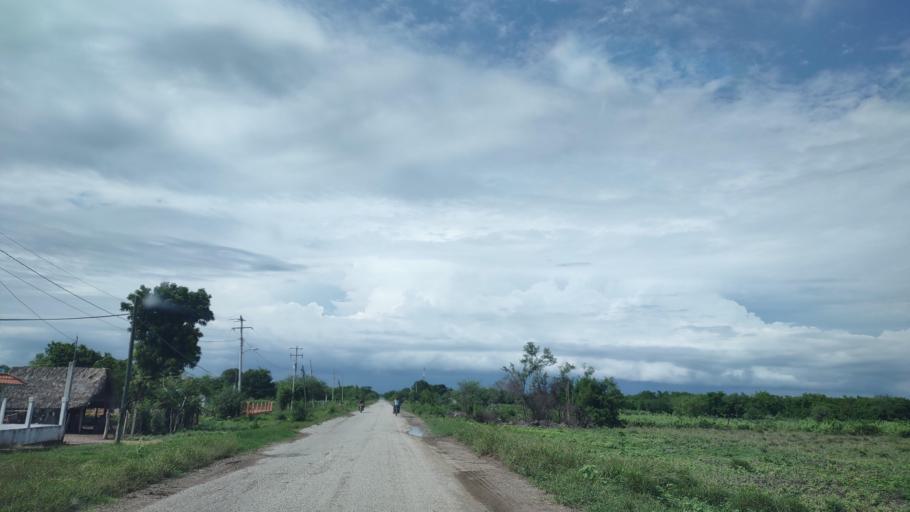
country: MX
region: Veracruz
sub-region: Panuco
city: Oviedo
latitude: 22.0065
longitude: -98.4624
